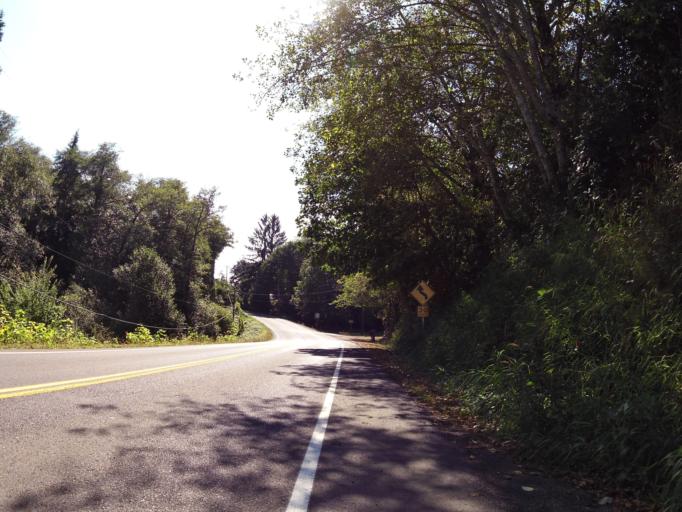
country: US
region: Washington
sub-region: Wahkiakum County
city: Cathlamet
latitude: 46.1821
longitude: -123.5837
